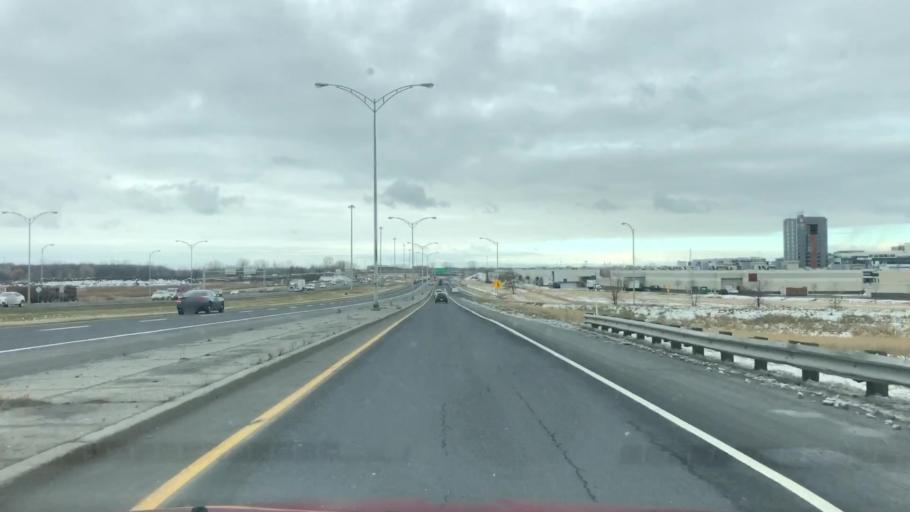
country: CA
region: Quebec
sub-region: Monteregie
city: Brossard
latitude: 45.4430
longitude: -73.4307
